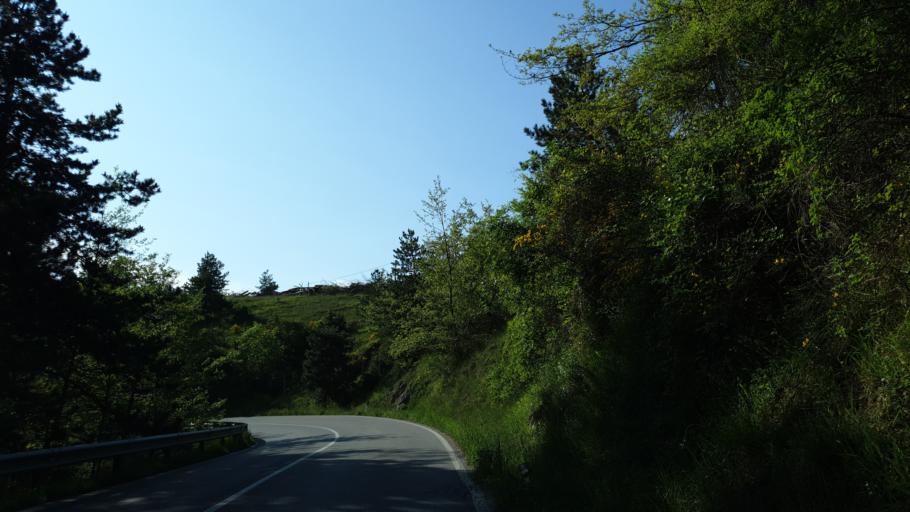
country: IT
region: Tuscany
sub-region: Province of Arezzo
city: Montemignaio
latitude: 43.7875
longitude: 11.6298
